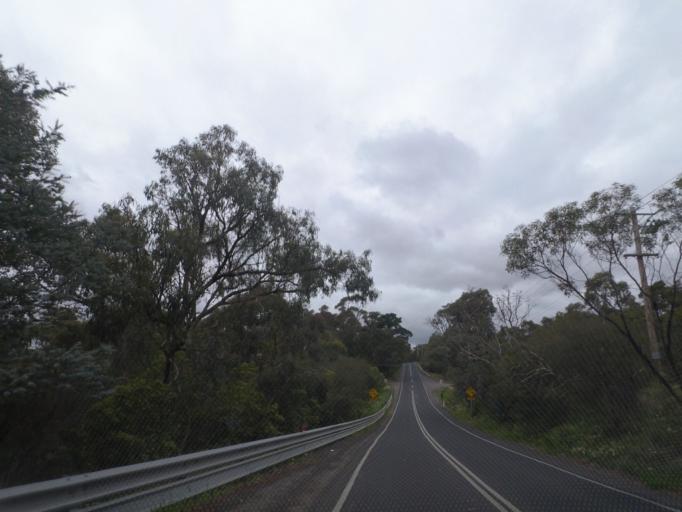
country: AU
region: Victoria
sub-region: Nillumbik
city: Hurstbridge
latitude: -37.6449
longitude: 145.2303
